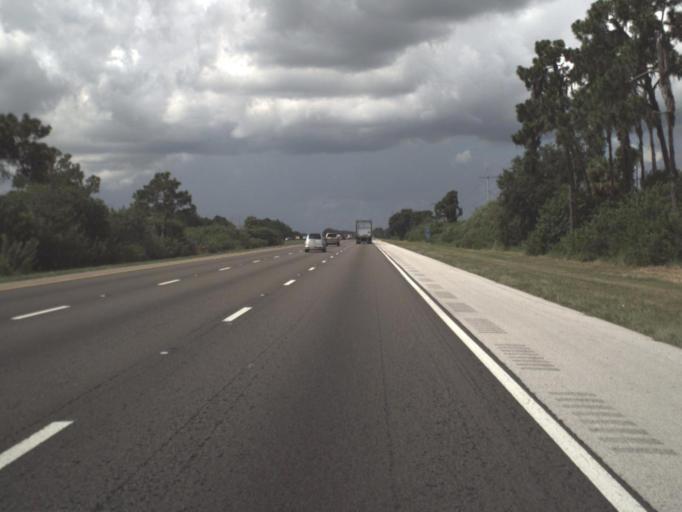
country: US
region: Florida
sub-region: Hillsborough County
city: Ruskin
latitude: 27.6782
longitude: -82.4259
